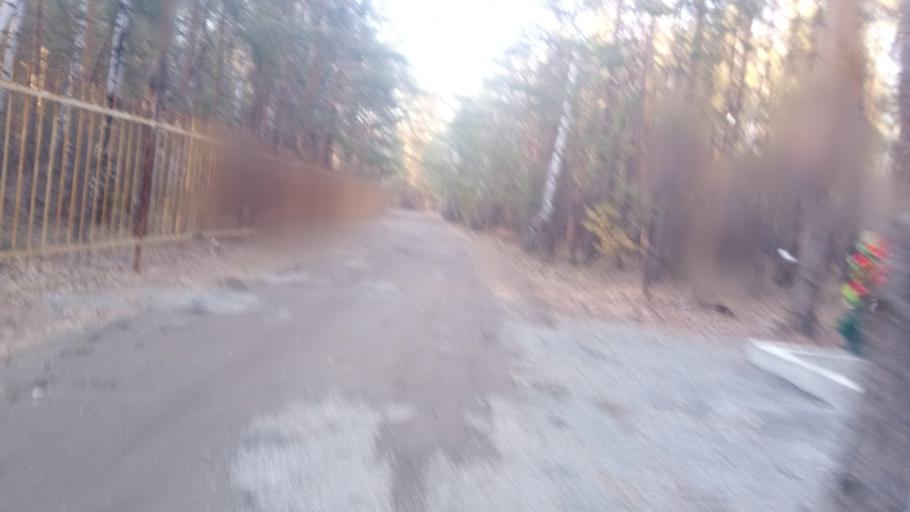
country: RU
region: Chelyabinsk
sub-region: Gorod Chelyabinsk
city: Chelyabinsk
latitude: 55.1268
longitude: 61.3474
